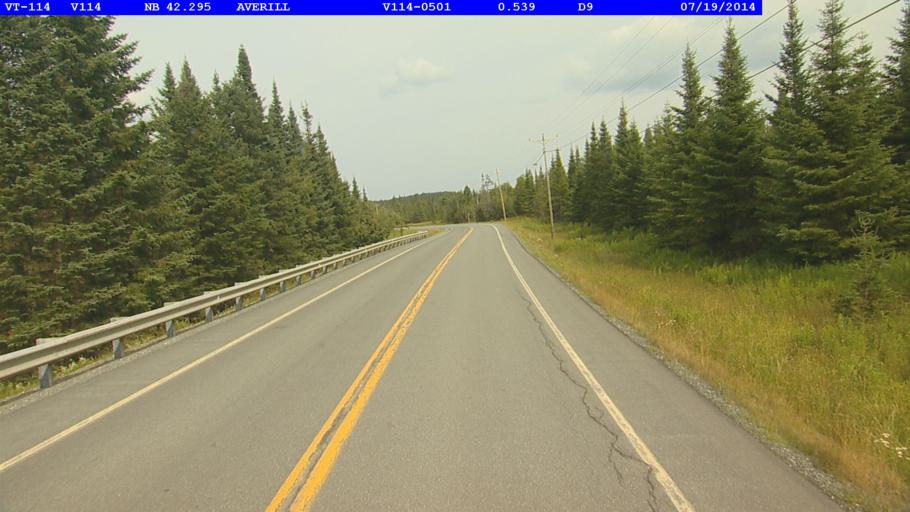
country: CA
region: Quebec
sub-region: Estrie
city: Coaticook
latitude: 45.0030
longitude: -71.6997
